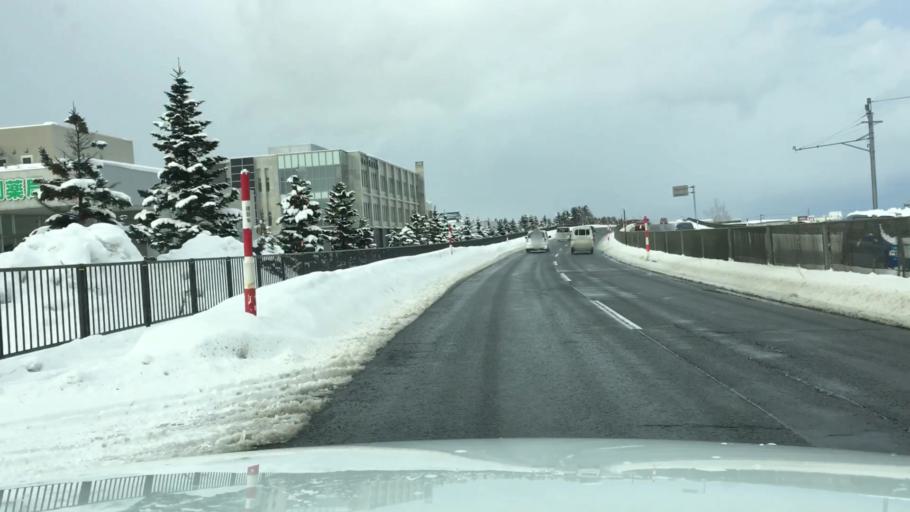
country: JP
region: Aomori
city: Hirosaki
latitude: 40.5865
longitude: 140.5072
